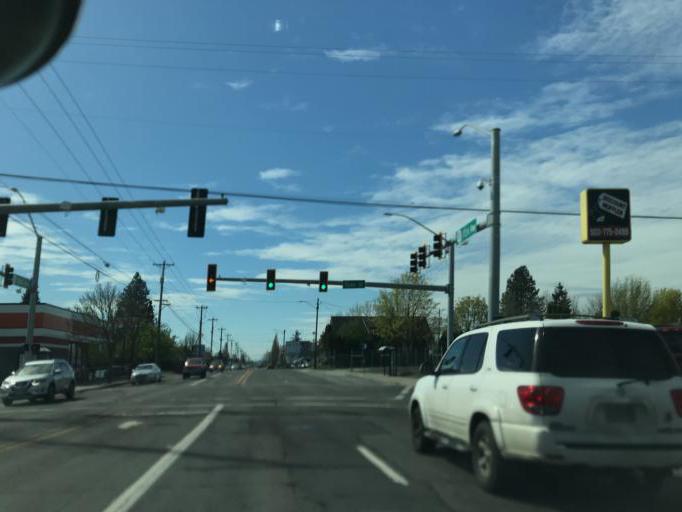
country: US
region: Oregon
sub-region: Multnomah County
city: Lents
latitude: 45.4763
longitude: -122.5791
